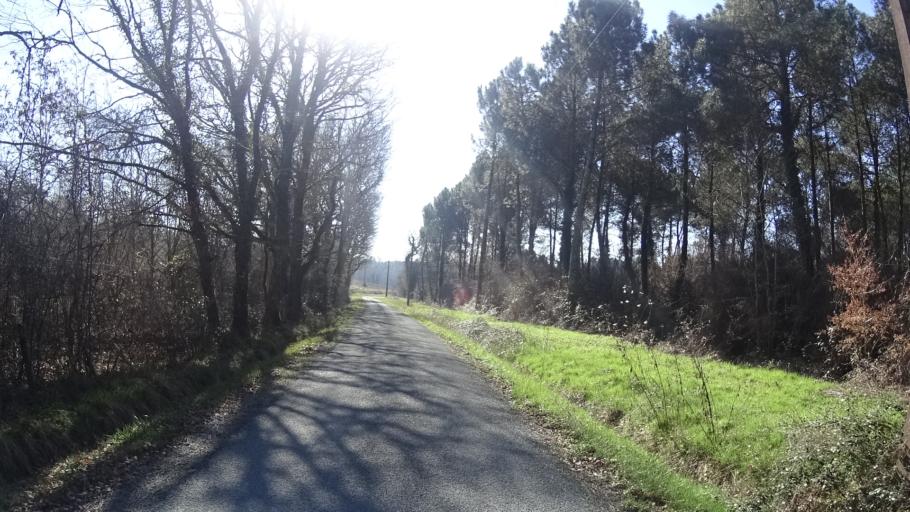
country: FR
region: Aquitaine
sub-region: Departement de la Dordogne
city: Montpon-Menesterol
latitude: 45.1025
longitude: 0.1978
